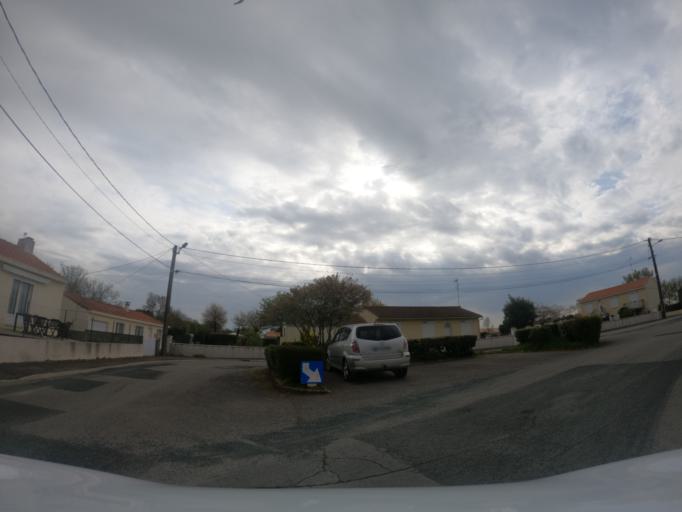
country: FR
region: Pays de la Loire
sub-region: Departement de la Vendee
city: Le Champ-Saint-Pere
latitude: 46.5098
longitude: -1.3398
